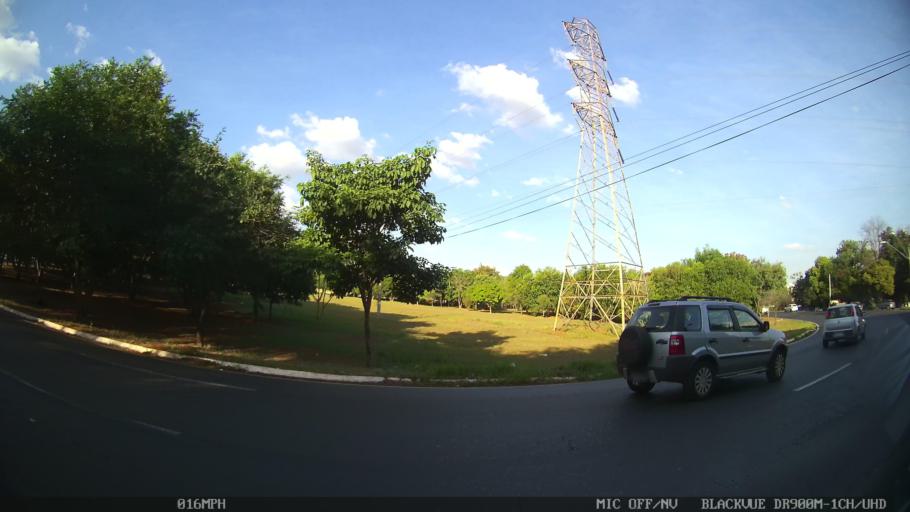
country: BR
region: Sao Paulo
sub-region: Ribeirao Preto
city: Ribeirao Preto
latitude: -21.1868
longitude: -47.7859
